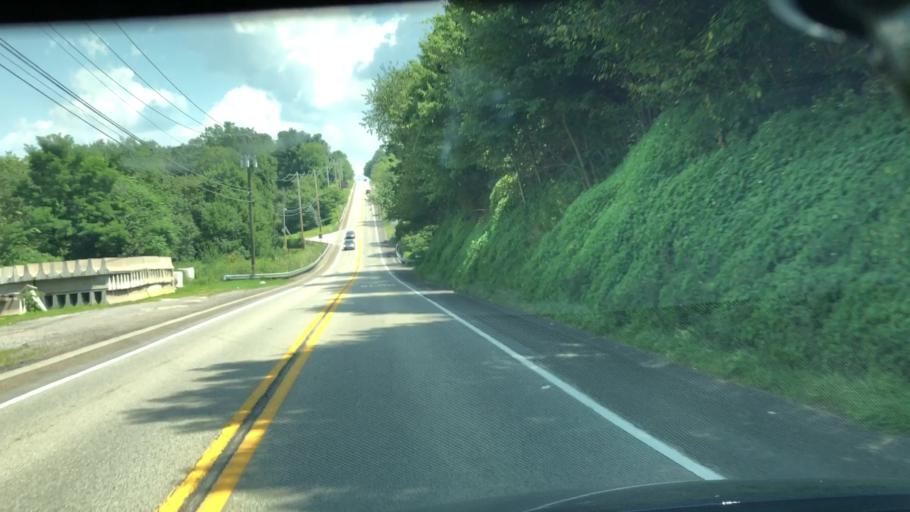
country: US
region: Pennsylvania
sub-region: Armstrong County
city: Freeport
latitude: 40.7103
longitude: -79.7363
